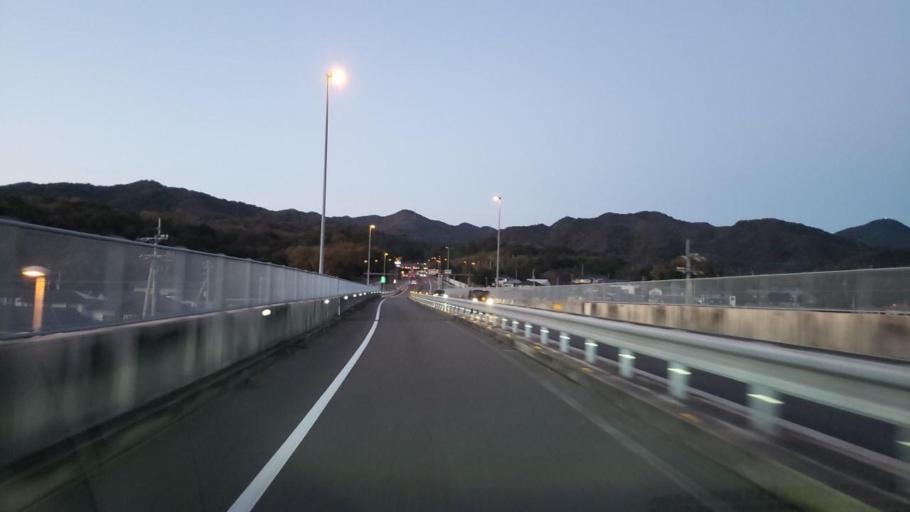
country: JP
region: Tokushima
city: Ishii
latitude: 34.1465
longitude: 134.4744
